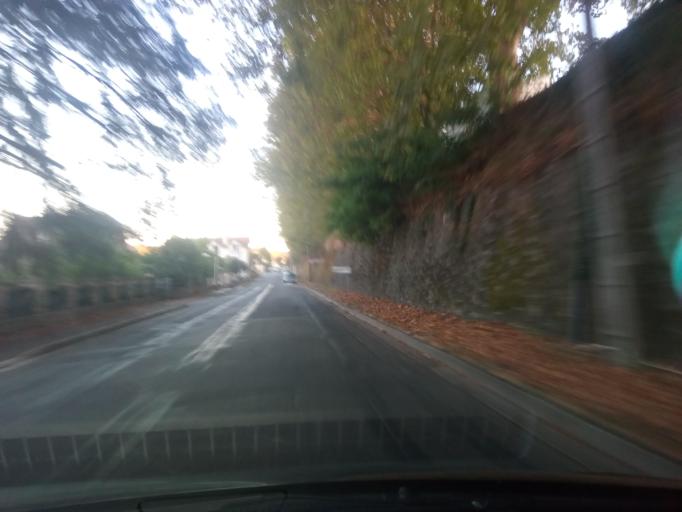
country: FR
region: Poitou-Charentes
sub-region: Departement de la Vienne
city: Montmorillon
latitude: 46.4170
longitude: 0.8752
